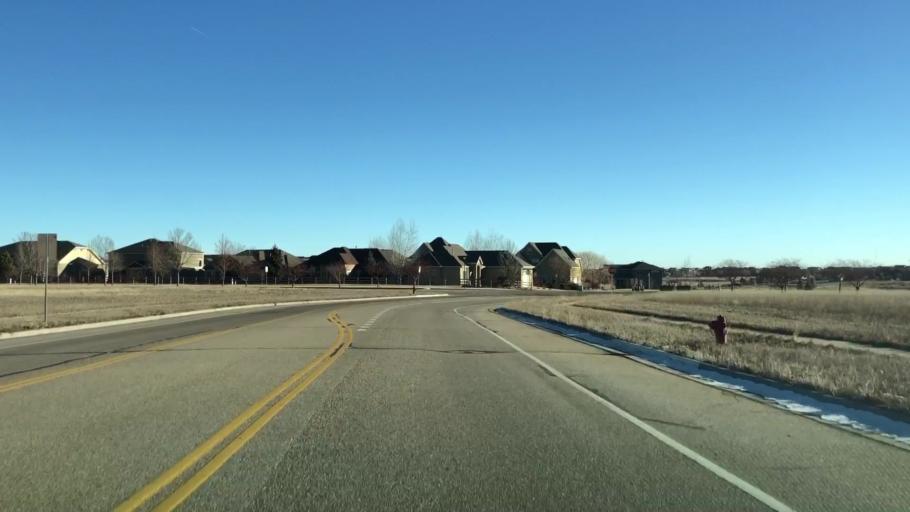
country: US
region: Colorado
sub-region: Weld County
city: Windsor
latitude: 40.4448
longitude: -104.9749
